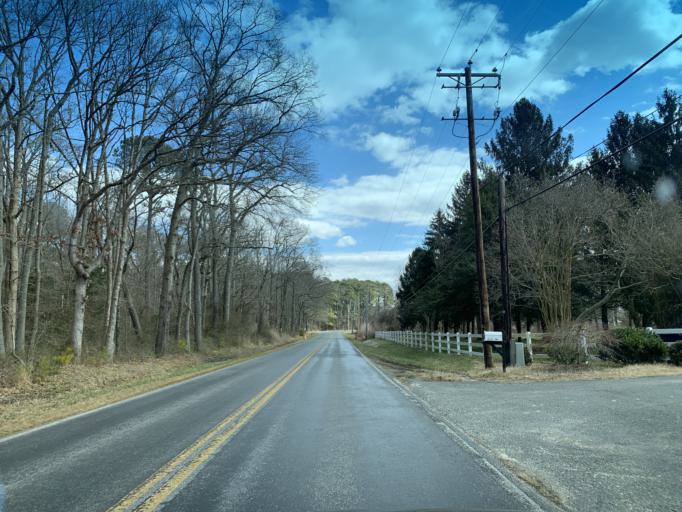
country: US
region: Maryland
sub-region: Queen Anne's County
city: Chester
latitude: 38.9445
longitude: -76.2681
